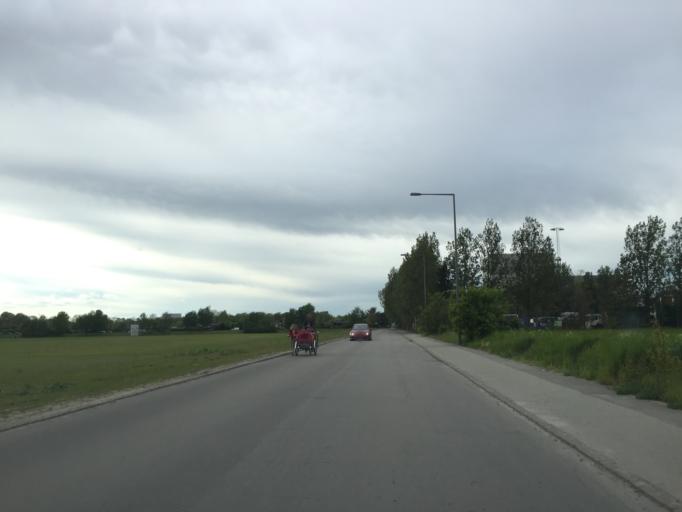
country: DK
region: Capital Region
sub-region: Kobenhavn
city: Christianshavn
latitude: 55.6727
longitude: 12.6184
